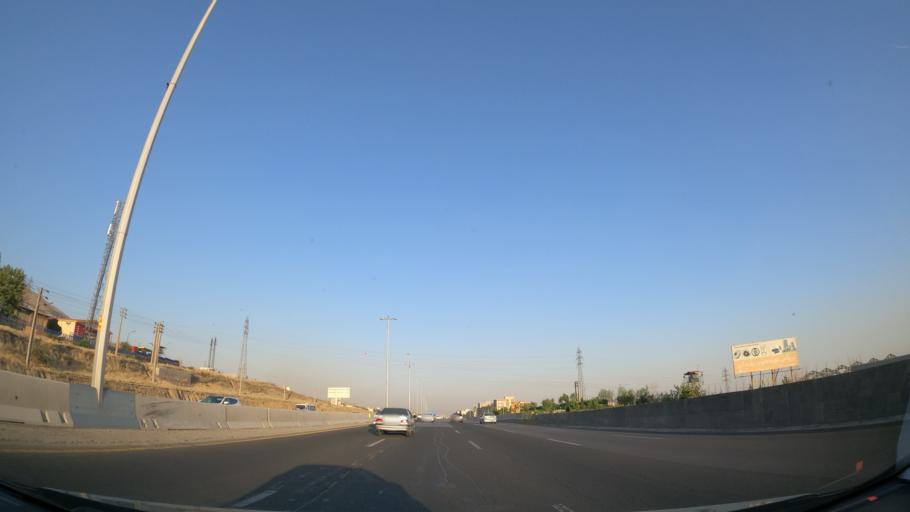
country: IR
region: Tehran
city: Shahr-e Qods
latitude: 35.7612
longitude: 51.0630
